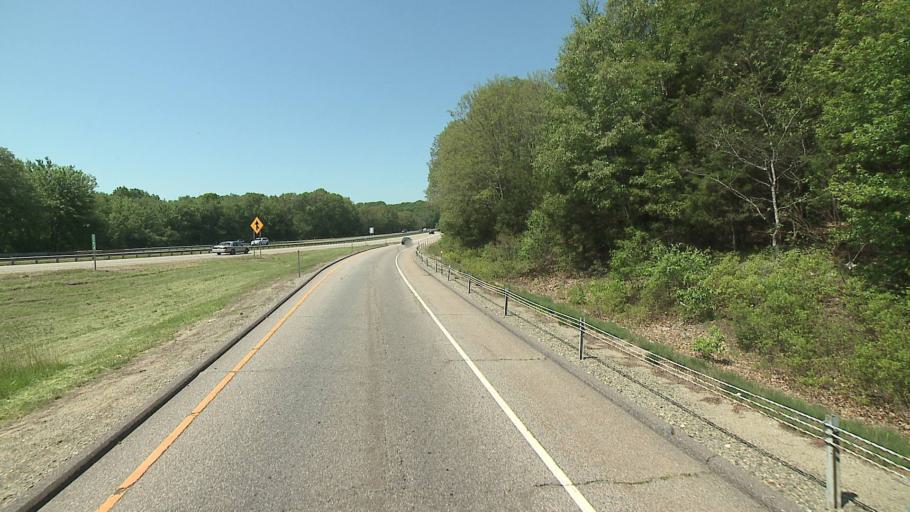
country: US
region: Connecticut
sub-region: New London County
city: Lisbon
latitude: 41.5892
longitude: -72.0233
